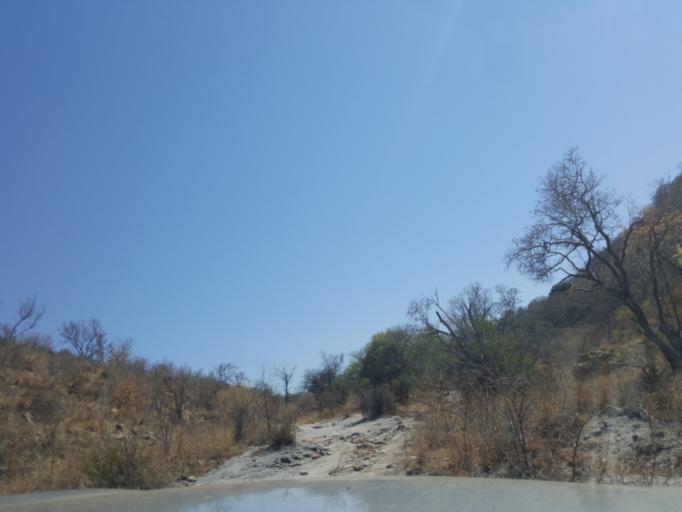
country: BW
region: South East
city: Lobatse
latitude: -25.1504
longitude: 25.6709
